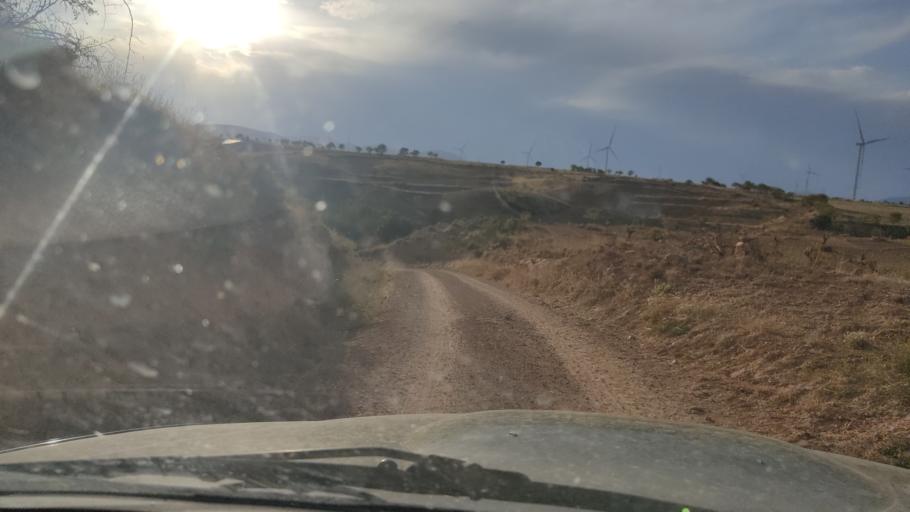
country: ES
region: Aragon
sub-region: Provincia de Teruel
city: Monforte de Moyuela
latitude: 41.0664
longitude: -0.9888
